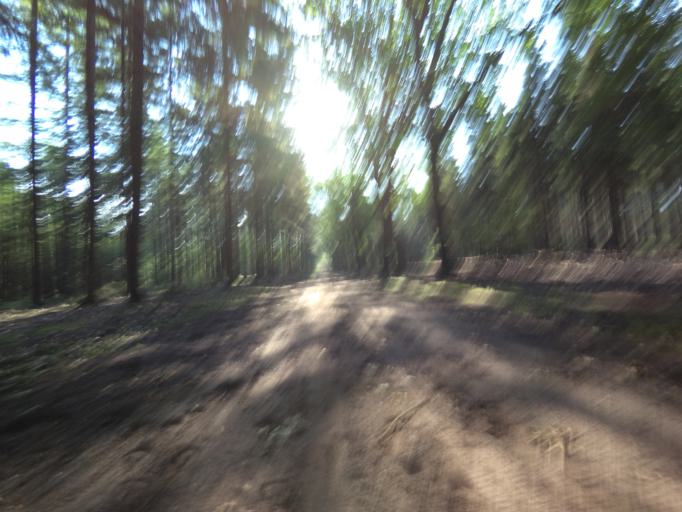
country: NL
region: Gelderland
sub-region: Gemeente Apeldoorn
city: Beekbergen
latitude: 52.1785
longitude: 5.8912
